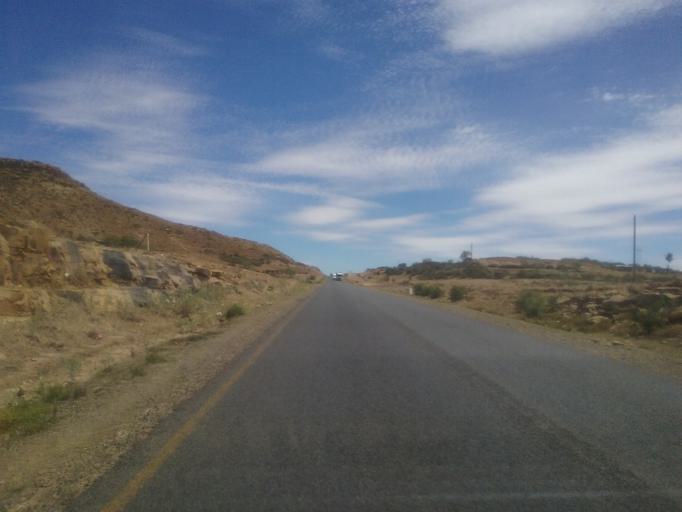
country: LS
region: Mohale's Hoek District
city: Mohale's Hoek
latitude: -30.0698
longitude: 27.4229
